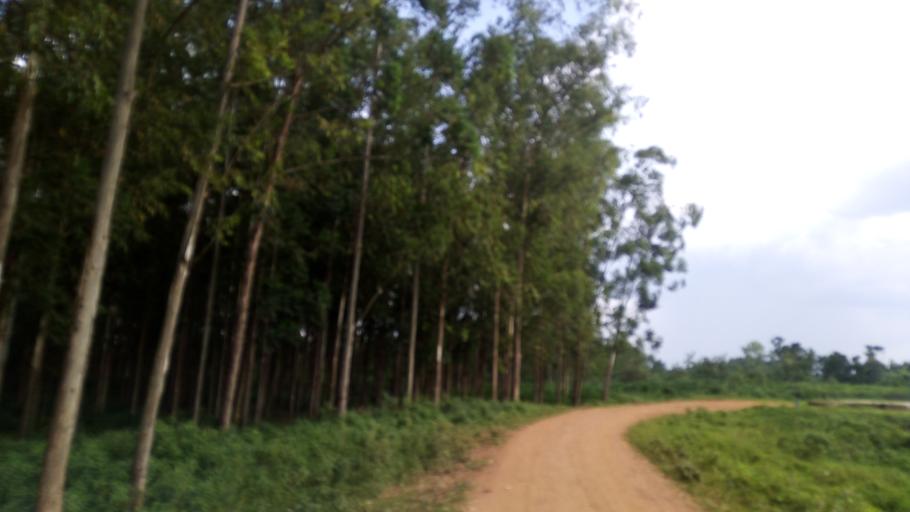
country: UG
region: Eastern Region
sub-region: Mbale District
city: Mbale
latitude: 1.0742
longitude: 34.1513
